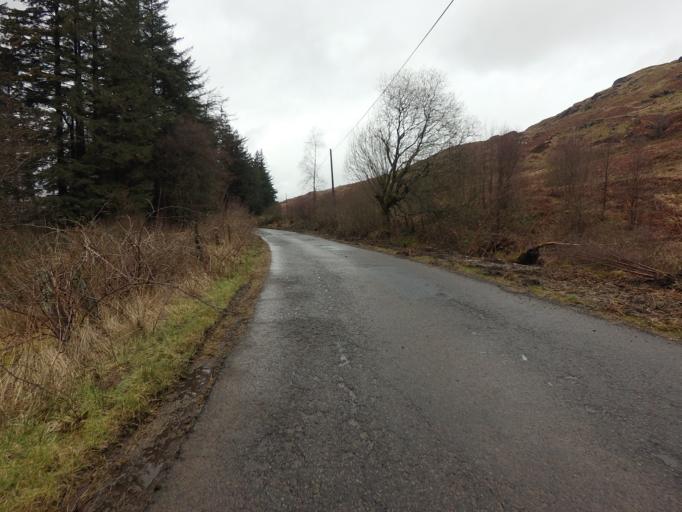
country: GB
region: Scotland
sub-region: Argyll and Bute
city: Garelochhead
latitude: 56.2495
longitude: -4.6453
